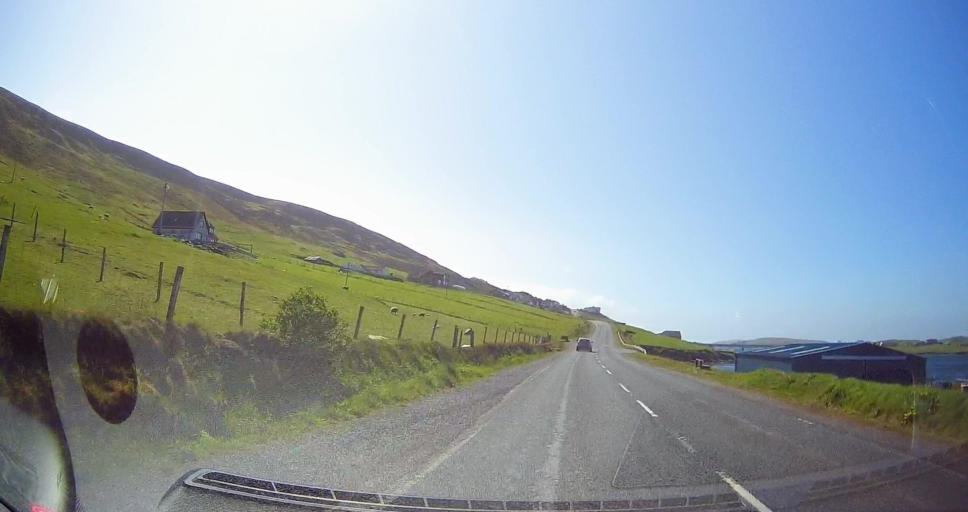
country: GB
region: Scotland
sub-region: Shetland Islands
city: Lerwick
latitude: 60.1362
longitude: -1.2666
